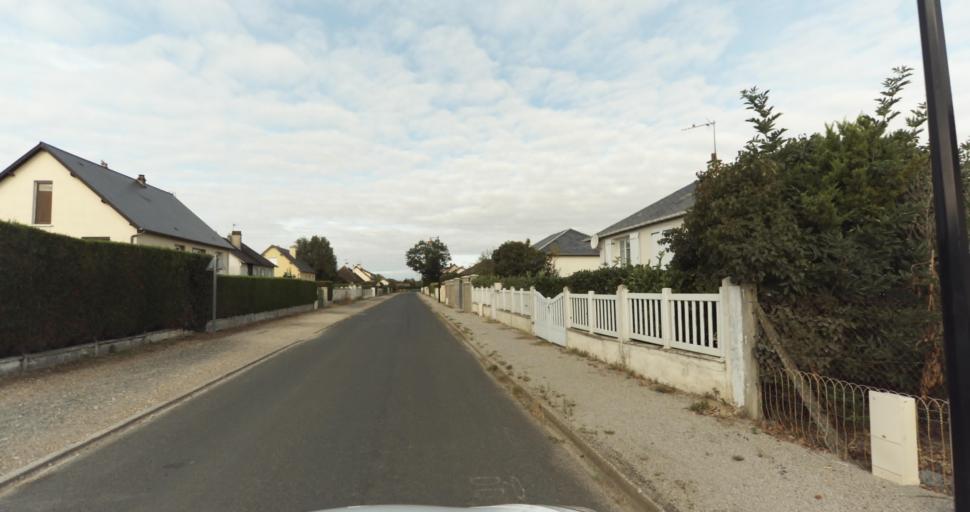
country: FR
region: Haute-Normandie
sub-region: Departement de l'Eure
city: Saint-Germain-sur-Avre
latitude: 48.8222
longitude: 1.2742
